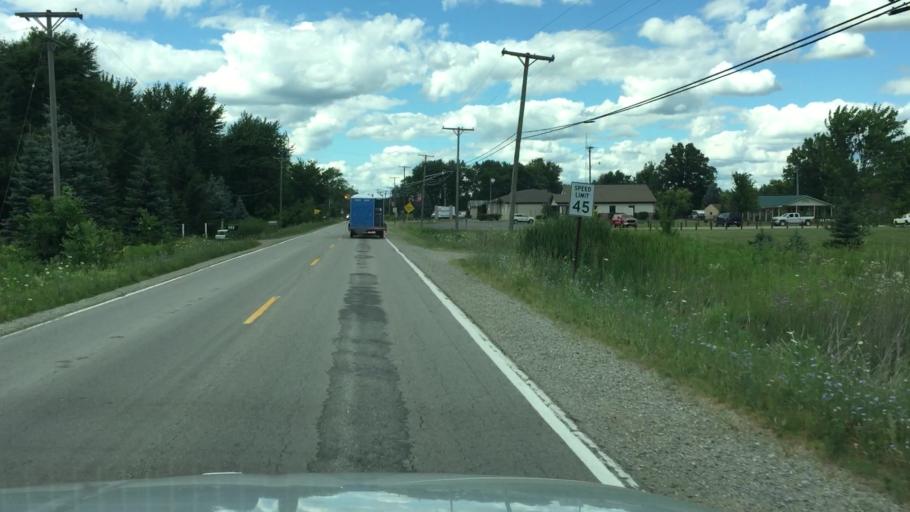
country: US
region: Michigan
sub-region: Macomb County
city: Armada
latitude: 42.9135
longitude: -82.9454
